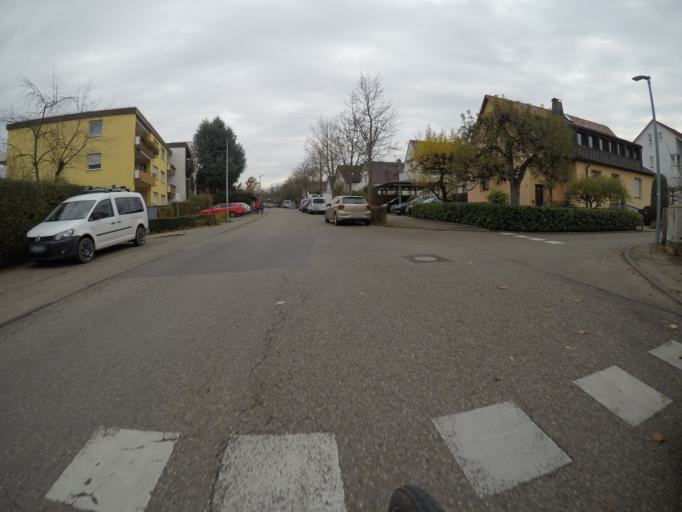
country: DE
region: Baden-Wuerttemberg
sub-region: Regierungsbezirk Stuttgart
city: Leinfelden-Echterdingen
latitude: 48.6921
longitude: 9.1384
